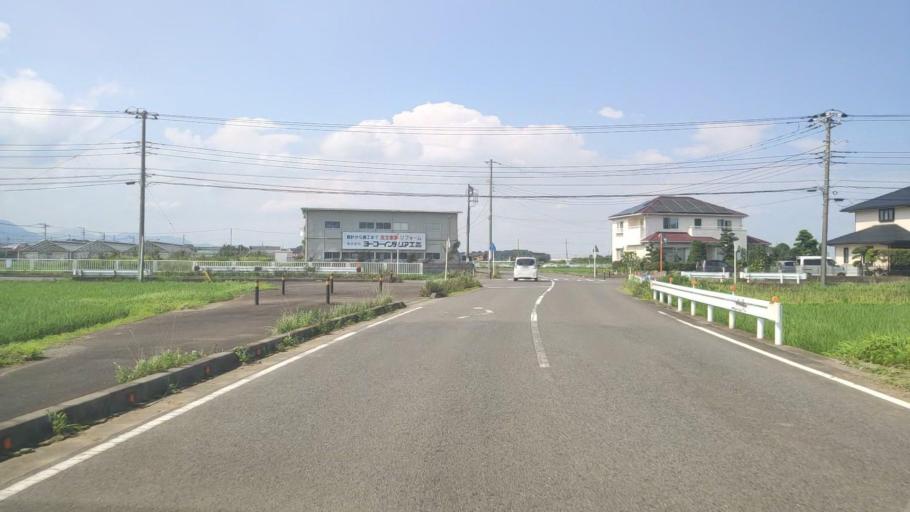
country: JP
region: Kanagawa
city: Isehara
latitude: 35.3631
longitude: 139.3165
